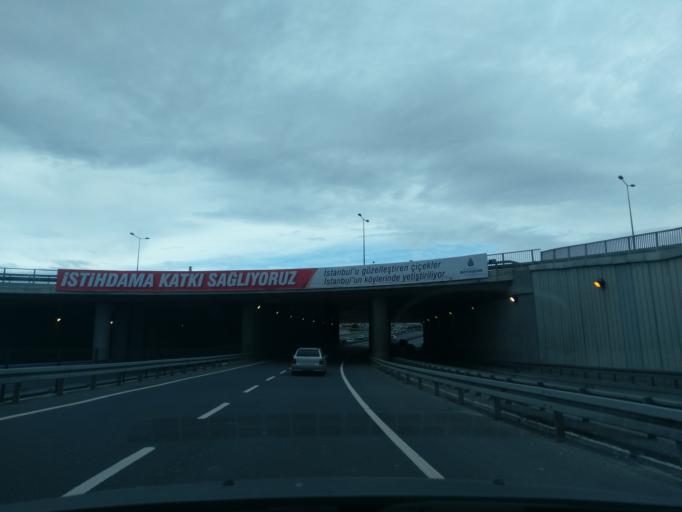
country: TR
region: Istanbul
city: Istanbul
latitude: 41.0013
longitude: 28.9448
